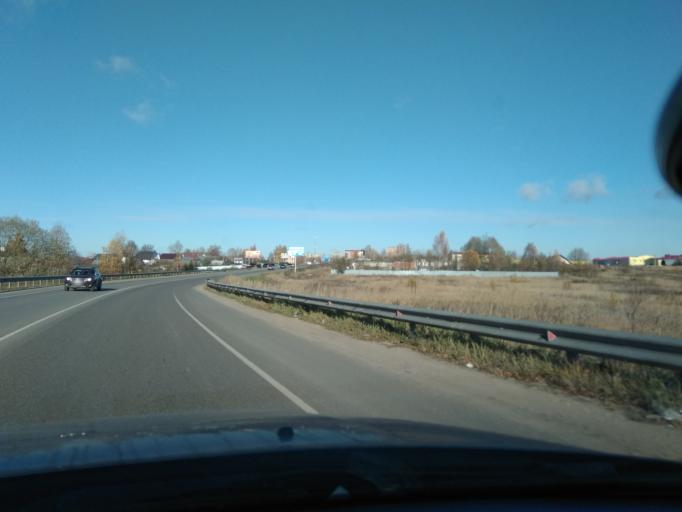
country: RU
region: Moskovskaya
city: Istra
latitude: 55.8942
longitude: 36.8635
